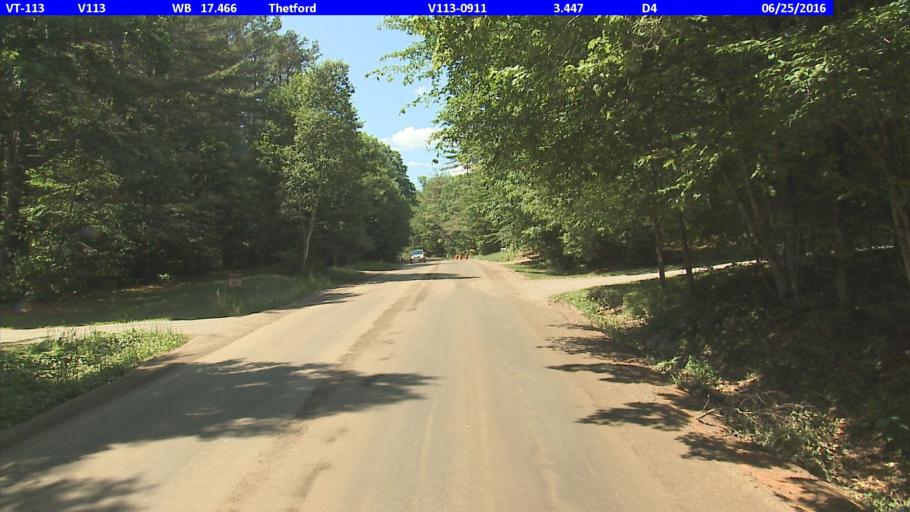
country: US
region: New Hampshire
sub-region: Grafton County
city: Lyme
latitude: 43.8500
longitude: -72.2557
